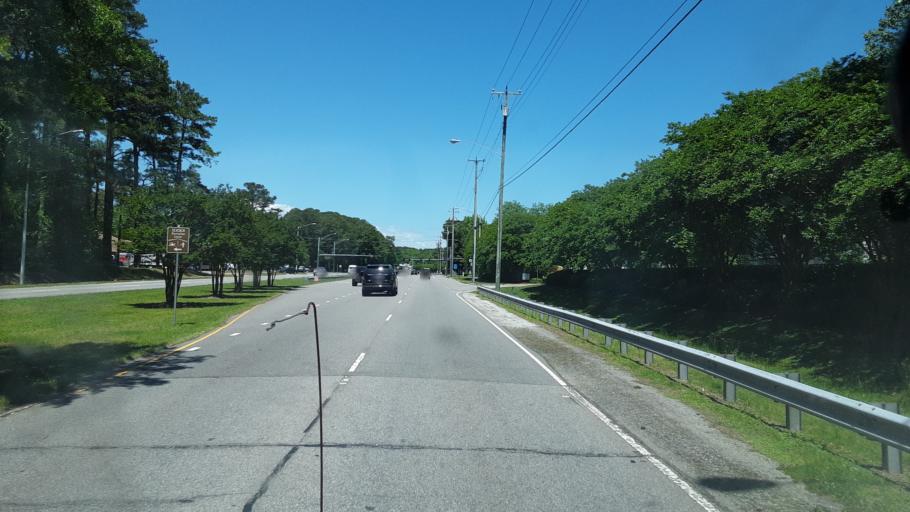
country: US
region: Virginia
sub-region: City of Virginia Beach
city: Virginia Beach
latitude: 36.8084
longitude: -75.9905
